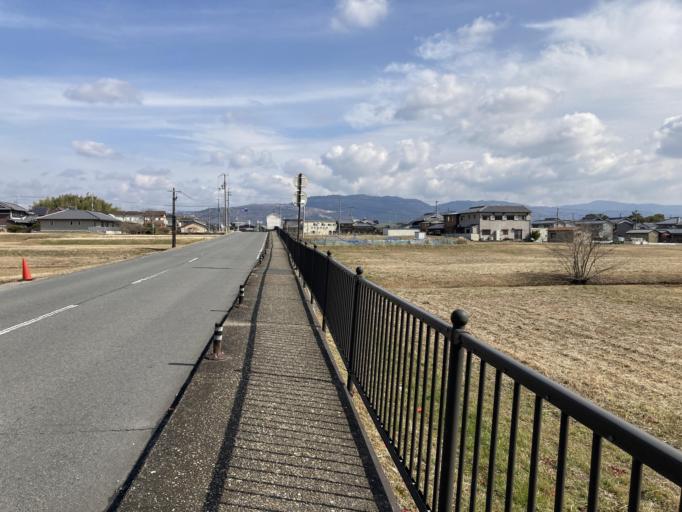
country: JP
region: Nara
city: Nara-shi
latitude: 34.6941
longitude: 135.8009
